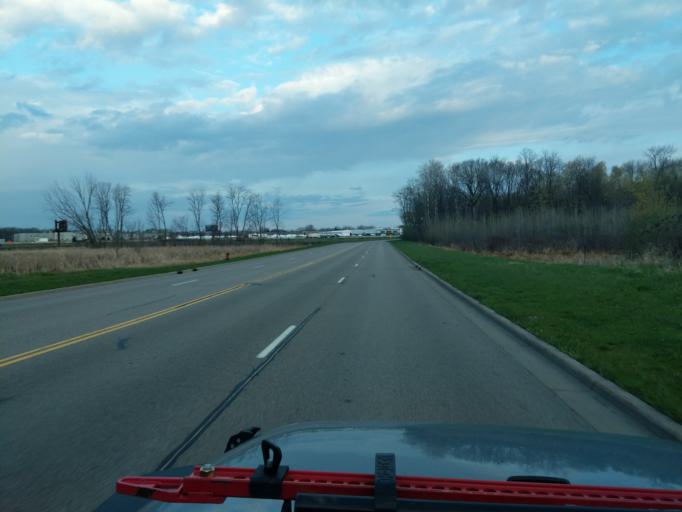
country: US
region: Minnesota
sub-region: Hennepin County
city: Rogers
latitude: 45.1832
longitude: -93.5299
